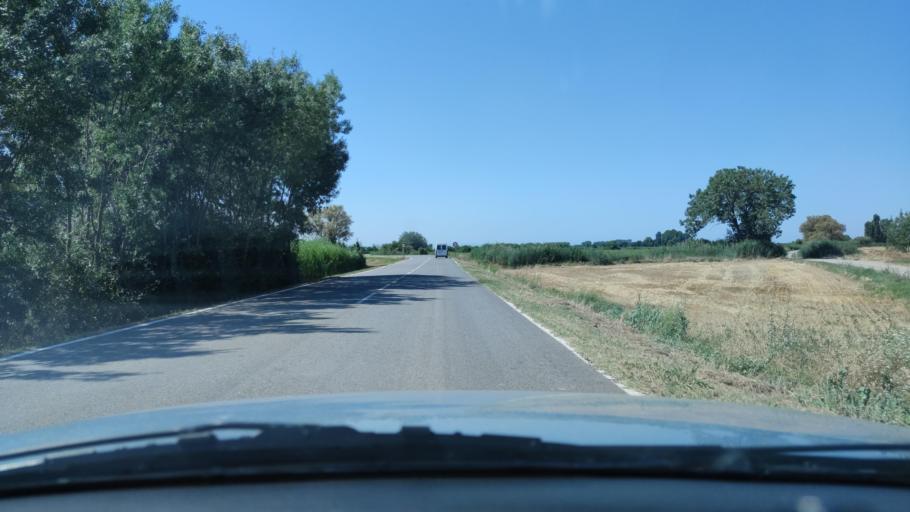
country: ES
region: Catalonia
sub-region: Provincia de Lleida
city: Castellsera
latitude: 41.7383
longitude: 0.9850
